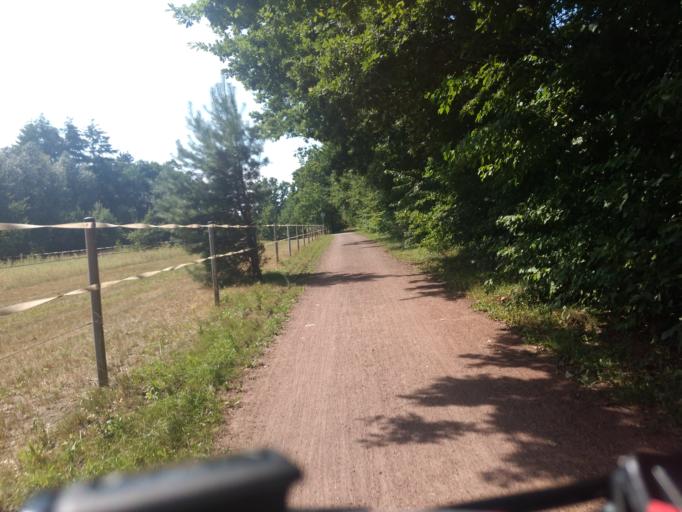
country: DE
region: North Rhine-Westphalia
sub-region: Regierungsbezirk Detmold
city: Hovelhof
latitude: 51.7668
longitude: 8.6553
